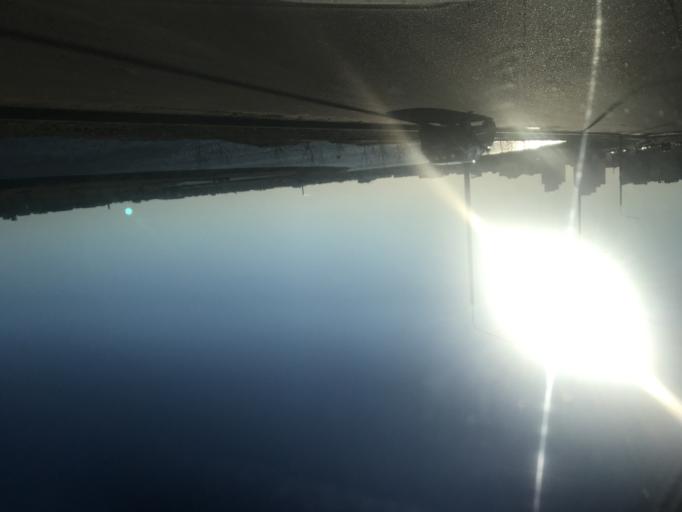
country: BY
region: Mogilev
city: Mahilyow
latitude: 53.8854
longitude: 30.3744
